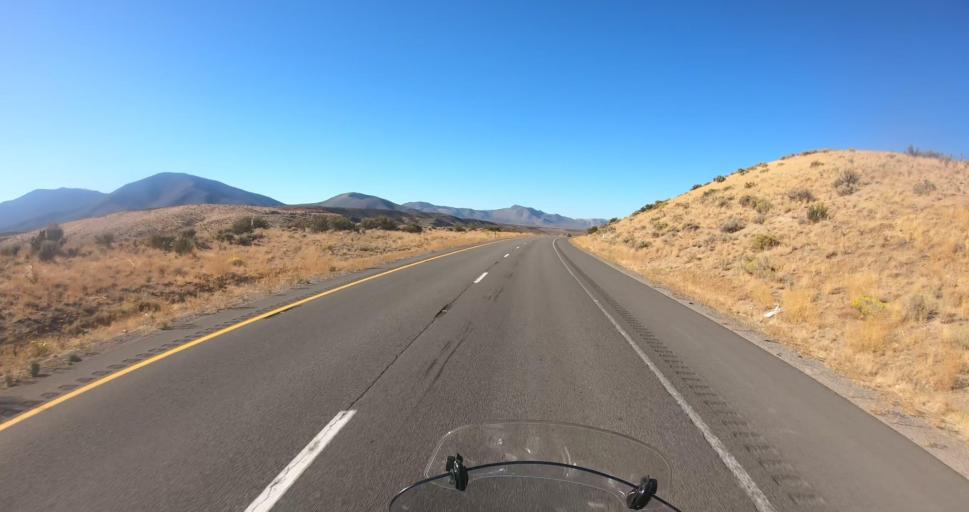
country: US
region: Nevada
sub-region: Washoe County
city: Cold Springs
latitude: 39.7011
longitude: -120.0310
